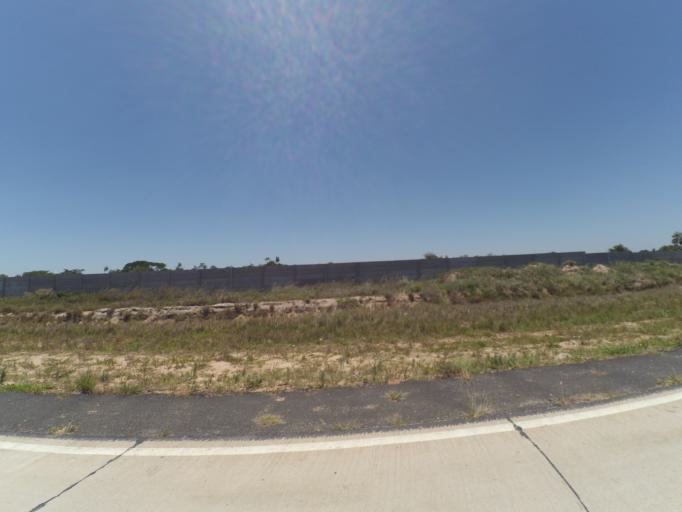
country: BO
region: Santa Cruz
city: Santa Cruz de la Sierra
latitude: -17.7895
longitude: -63.2741
